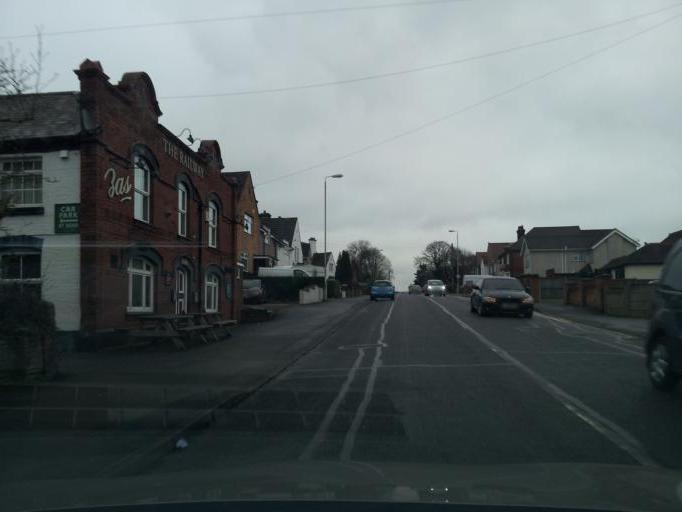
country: GB
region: England
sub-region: Leicestershire
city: Donisthorpe
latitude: 52.7375
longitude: -1.5331
